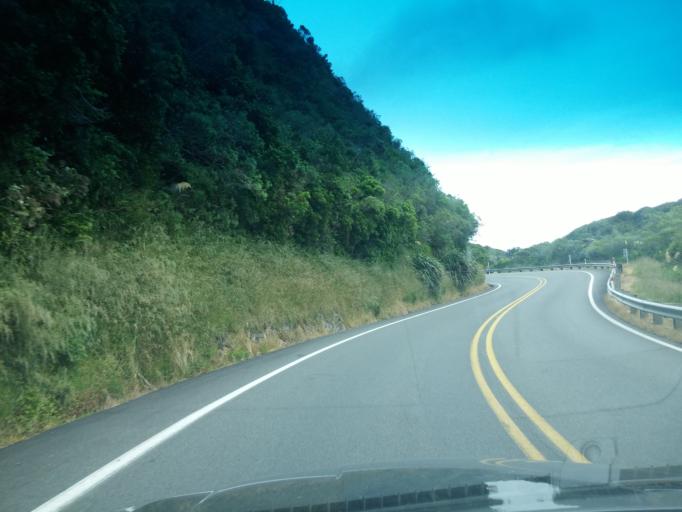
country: NZ
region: Wellington
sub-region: Upper Hutt City
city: Upper Hutt
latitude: -41.1140
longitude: 175.2384
